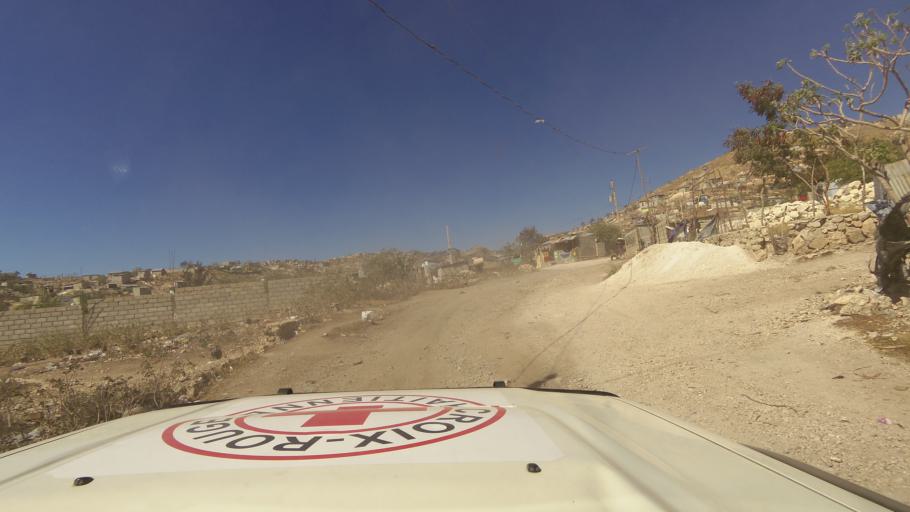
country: HT
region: Ouest
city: Croix des Bouquets
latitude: 18.6626
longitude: -72.2658
